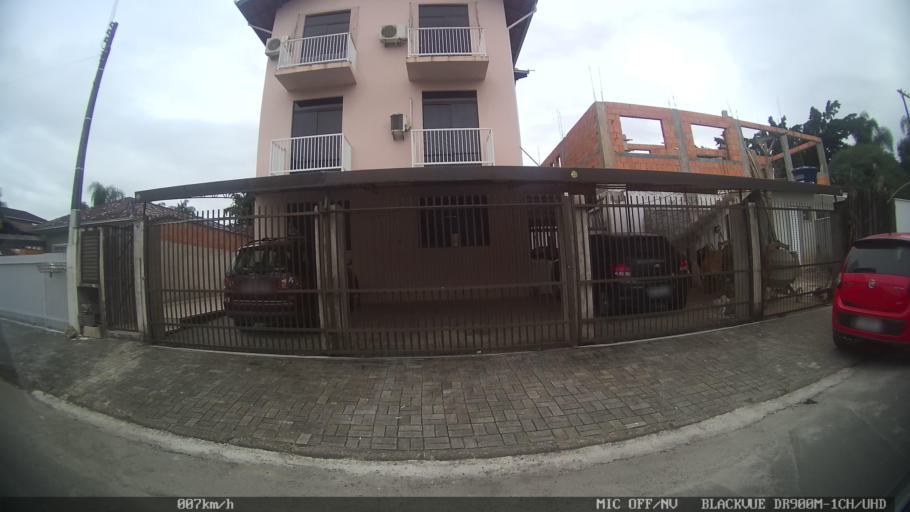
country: BR
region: Santa Catarina
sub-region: Joinville
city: Joinville
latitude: -26.2689
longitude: -48.8706
